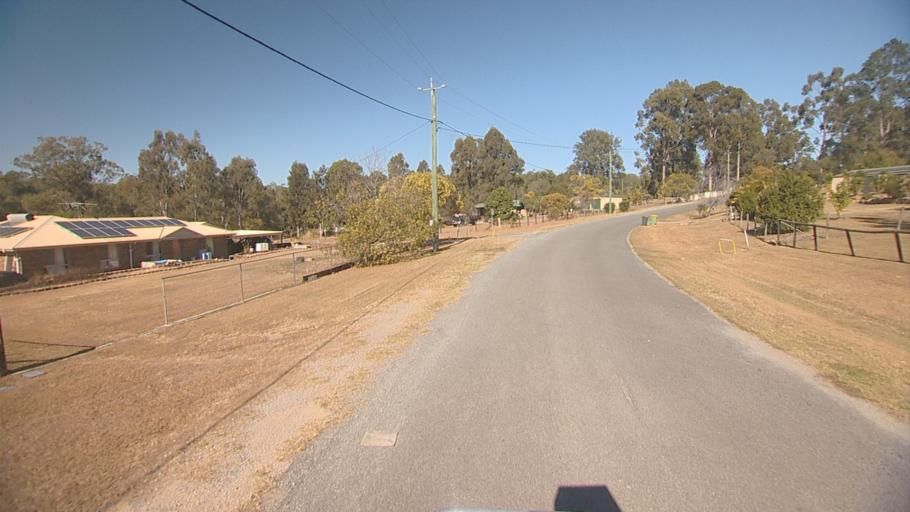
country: AU
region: Queensland
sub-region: Logan
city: Cedar Vale
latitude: -27.8699
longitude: 153.0067
